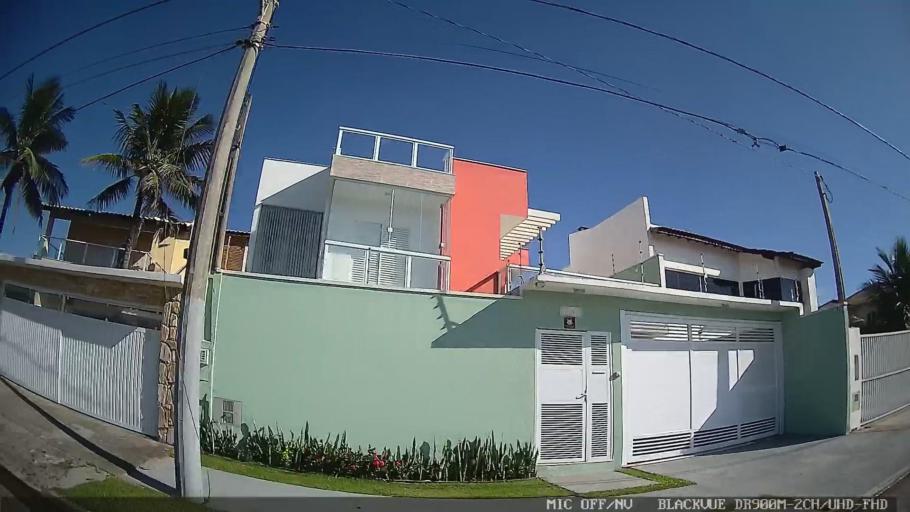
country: BR
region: Sao Paulo
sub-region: Peruibe
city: Peruibe
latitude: -24.2829
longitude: -46.9459
